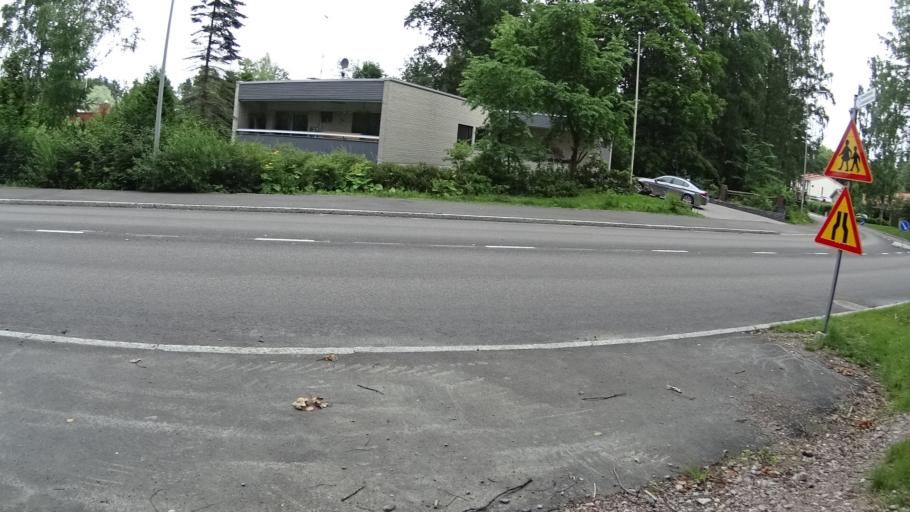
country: FI
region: Uusimaa
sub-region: Helsinki
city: Teekkarikylae
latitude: 60.2254
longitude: 24.8357
